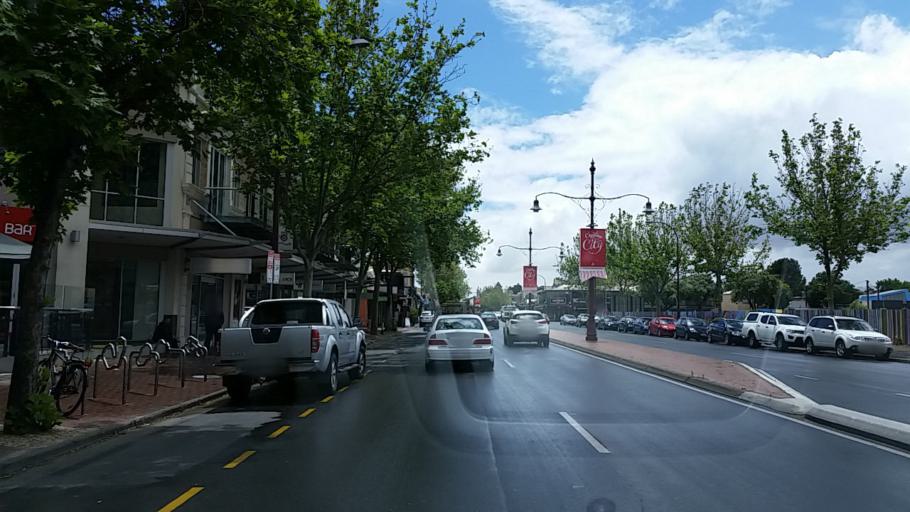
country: AU
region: South Australia
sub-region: Adelaide
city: North Adelaide
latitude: -34.9071
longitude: 138.5962
